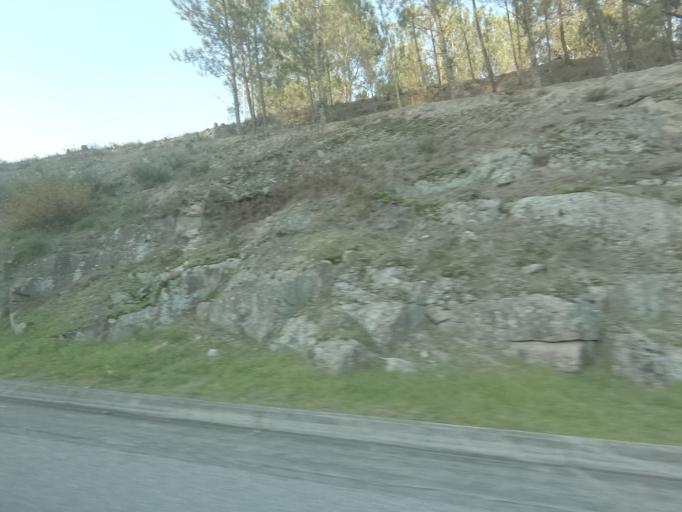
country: PT
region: Porto
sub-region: Amarante
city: Figueiro
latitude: 41.2368
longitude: -8.1891
